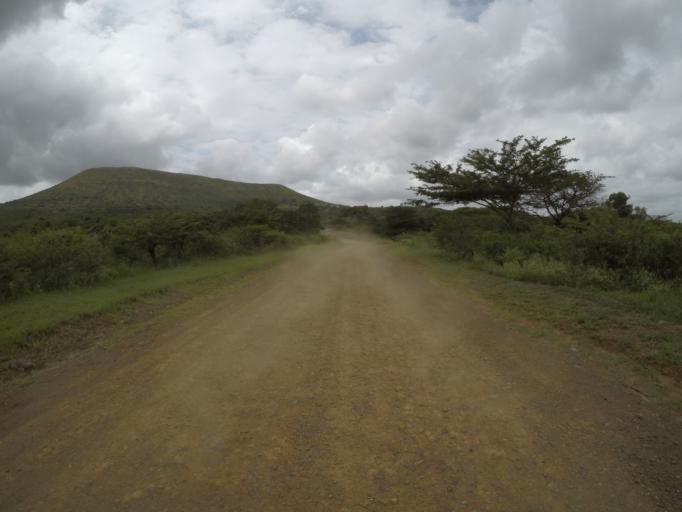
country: ZA
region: KwaZulu-Natal
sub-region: uThungulu District Municipality
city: Empangeni
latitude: -28.5953
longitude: 31.8911
